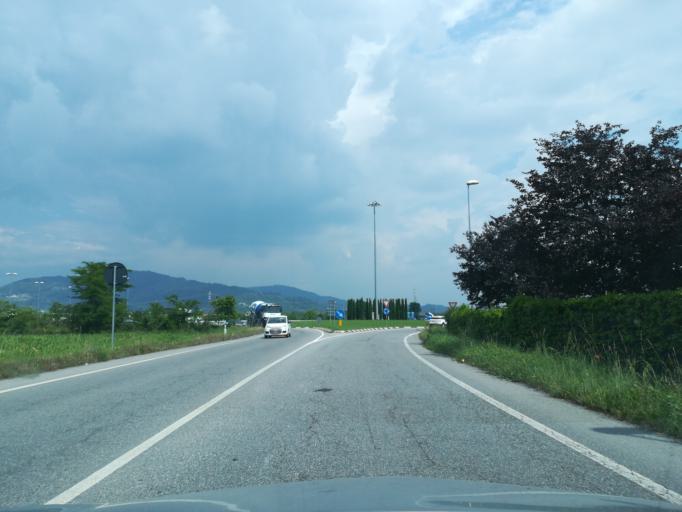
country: IT
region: Lombardy
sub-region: Provincia di Bergamo
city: Costa di Mezzate
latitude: 45.6558
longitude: 9.8068
